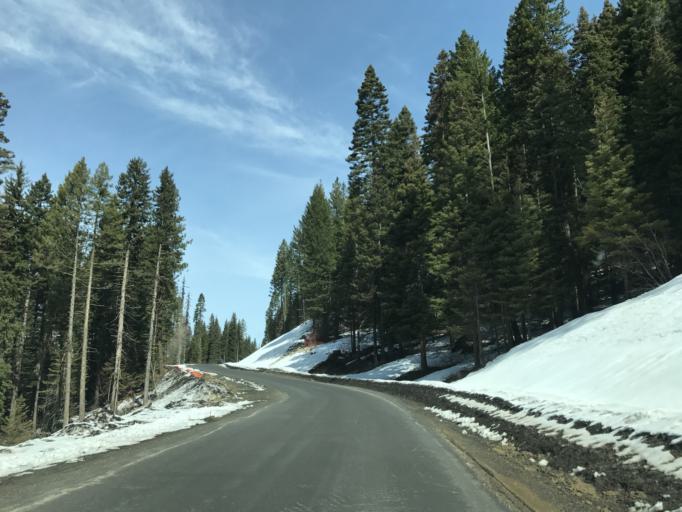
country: US
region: Idaho
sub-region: Valley County
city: McCall
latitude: 44.9906
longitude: -116.1656
